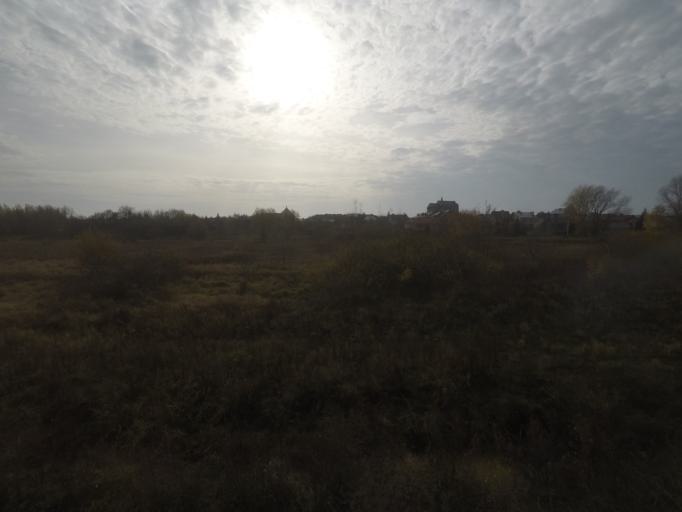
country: PL
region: Subcarpathian Voivodeship
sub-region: Powiat ropczycko-sedziszowski
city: Sedziszow Malopolski
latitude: 50.0748
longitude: 21.7047
